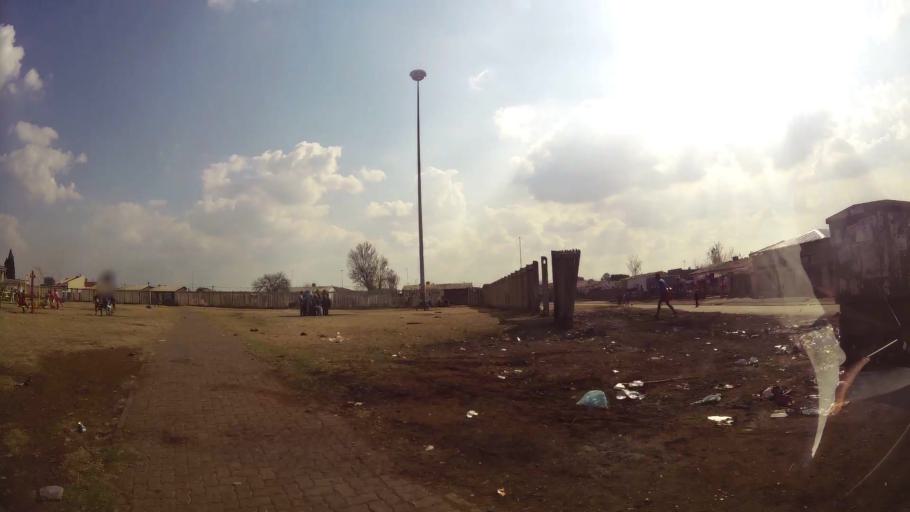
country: ZA
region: Gauteng
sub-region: Ekurhuleni Metropolitan Municipality
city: Germiston
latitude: -26.3066
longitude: 28.1504
